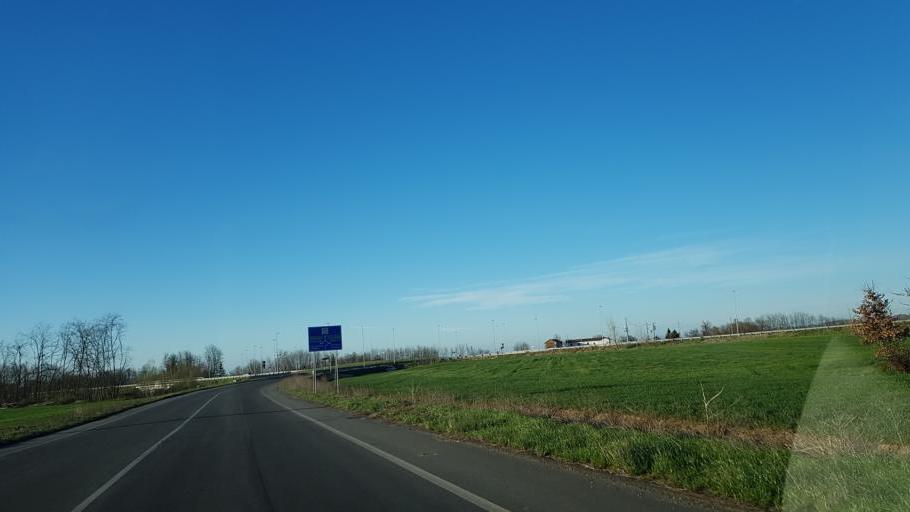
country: IT
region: Piedmont
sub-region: Provincia di Alessandria
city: Serravalle Scrivia
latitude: 44.7422
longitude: 8.8354
